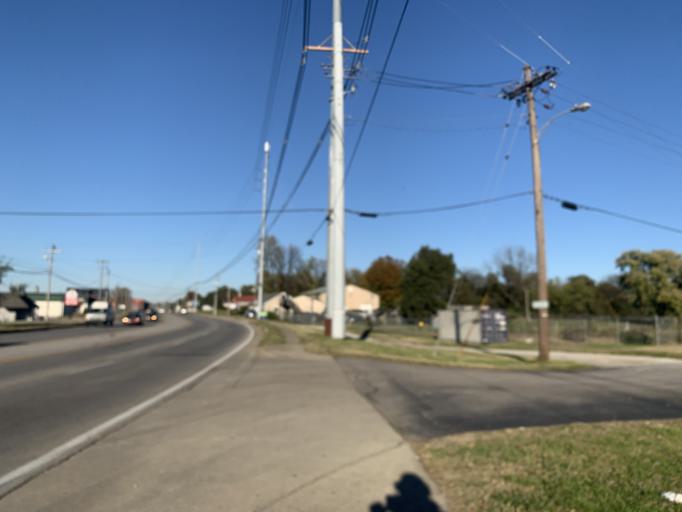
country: US
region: Kentucky
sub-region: Jefferson County
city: Shively
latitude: 38.2030
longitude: -85.7919
